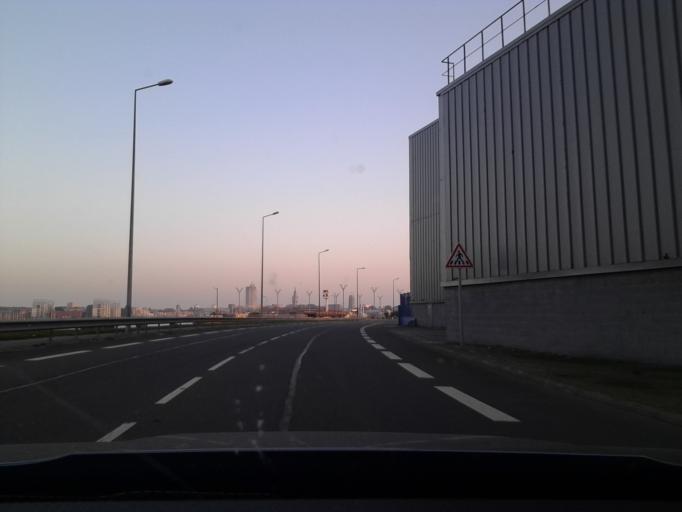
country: FR
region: Nord-Pas-de-Calais
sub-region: Departement du Nord
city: Dunkerque
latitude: 51.0504
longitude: 2.3637
